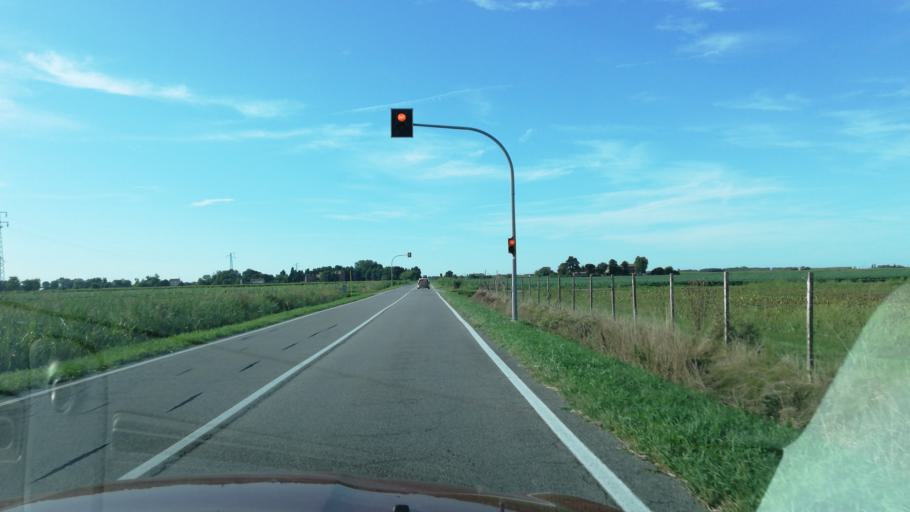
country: IT
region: Veneto
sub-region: Provincia di Venezia
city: La Salute di Livenza
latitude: 45.6085
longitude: 12.8034
